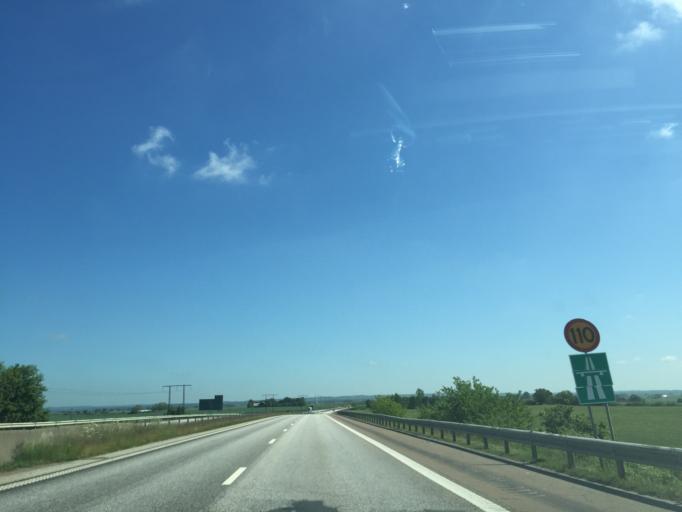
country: SE
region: Skane
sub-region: Astorps Kommun
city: Astorp
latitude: 56.1510
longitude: 12.9440
